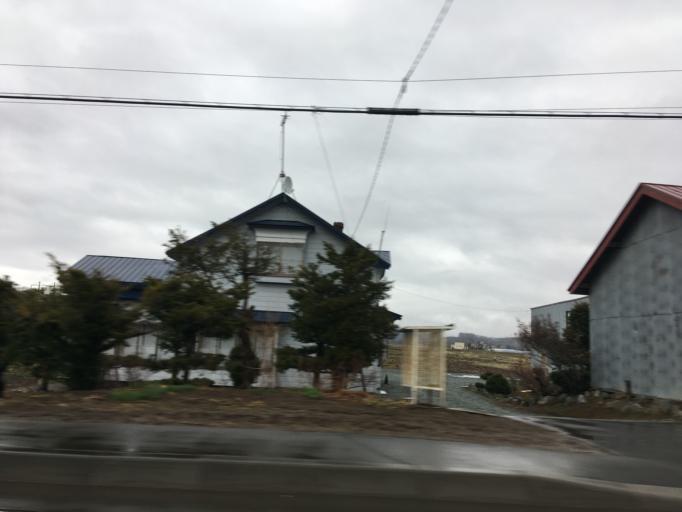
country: JP
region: Hokkaido
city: Nayoro
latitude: 44.1167
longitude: 142.4809
